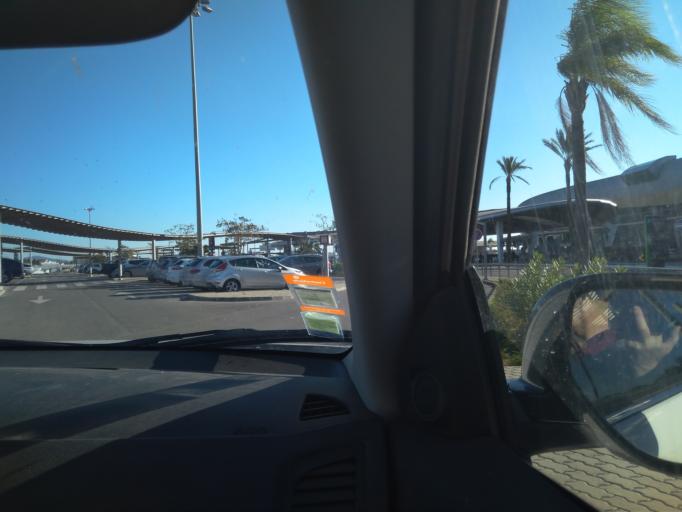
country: PT
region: Faro
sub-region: Faro
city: Faro
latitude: 37.0211
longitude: -7.9702
